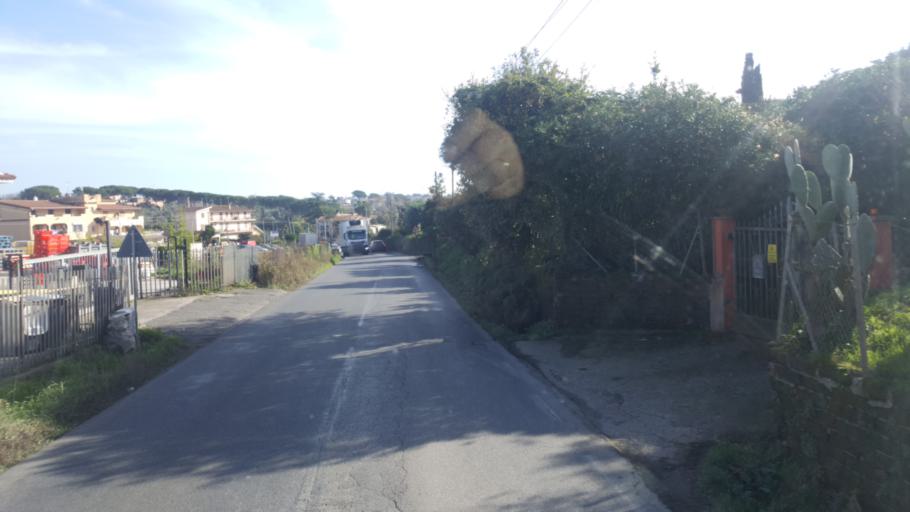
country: IT
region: Latium
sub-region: Citta metropolitana di Roma Capitale
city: Mantiglia di Ardea
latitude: 41.6802
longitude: 12.6213
